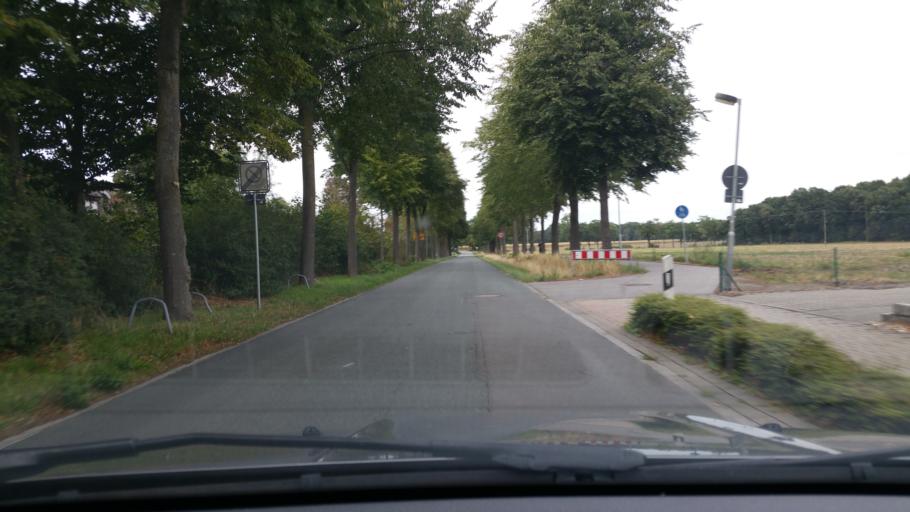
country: DE
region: North Rhine-Westphalia
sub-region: Regierungsbezirk Dusseldorf
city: Bocholt
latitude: 51.8578
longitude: 6.6323
